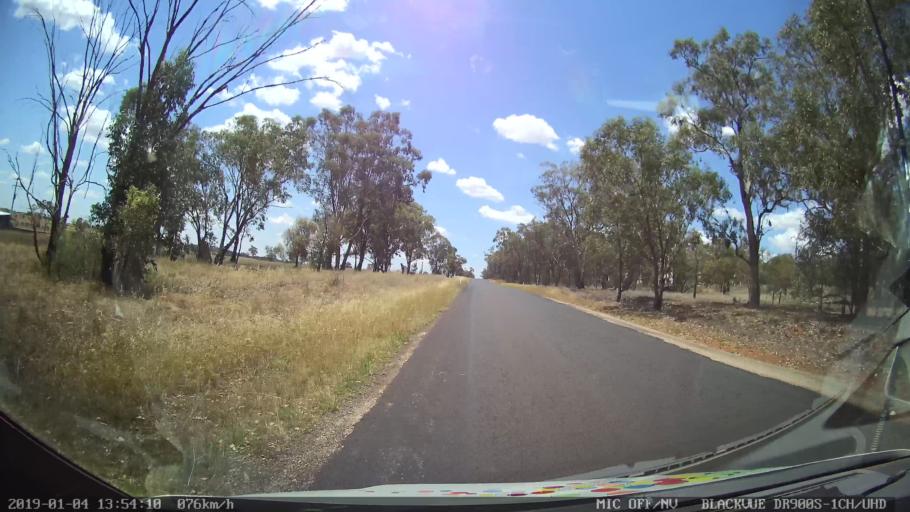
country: AU
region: New South Wales
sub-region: Dubbo Municipality
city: Dubbo
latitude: -32.3757
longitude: 148.5790
